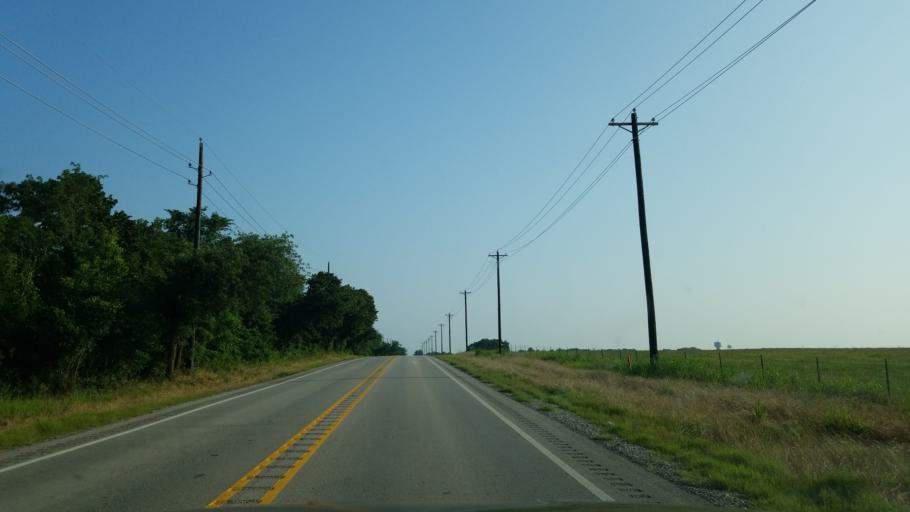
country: US
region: Texas
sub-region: Denton County
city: Aubrey
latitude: 33.3186
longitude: -96.9757
